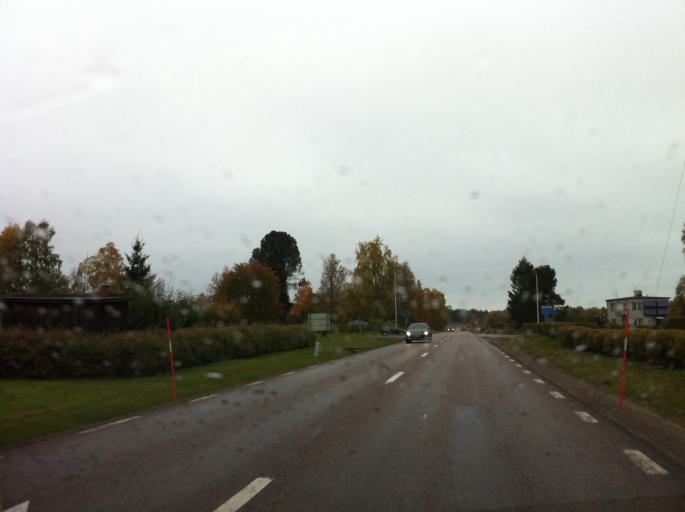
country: SE
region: Dalarna
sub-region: Ludvika Kommun
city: Grangesberg
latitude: 60.2505
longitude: 14.9794
